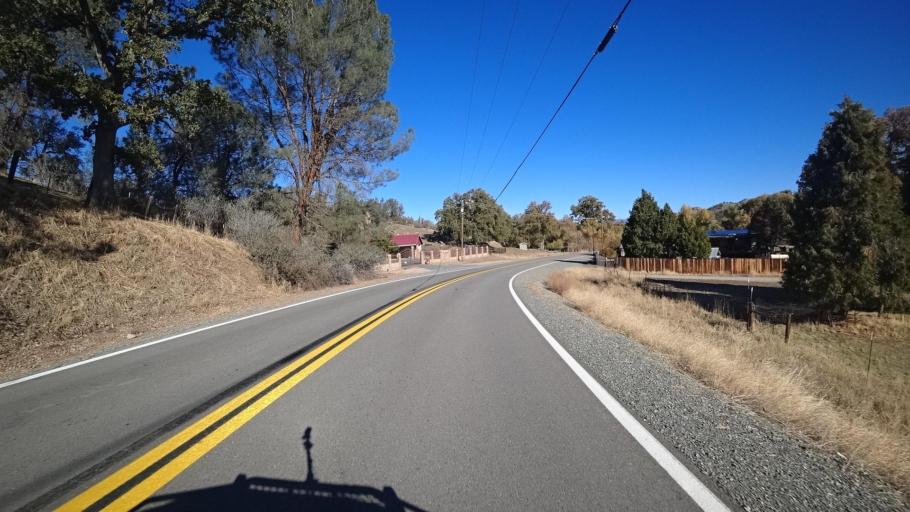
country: US
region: California
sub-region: Kern County
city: Alta Sierra
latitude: 35.7213
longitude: -118.7244
